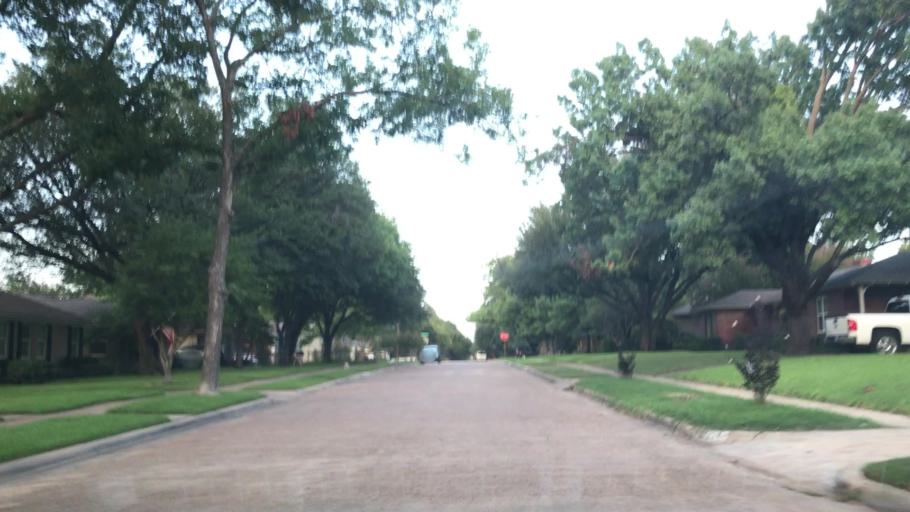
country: US
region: Texas
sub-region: Dallas County
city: Highland Park
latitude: 32.8392
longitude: -96.7563
